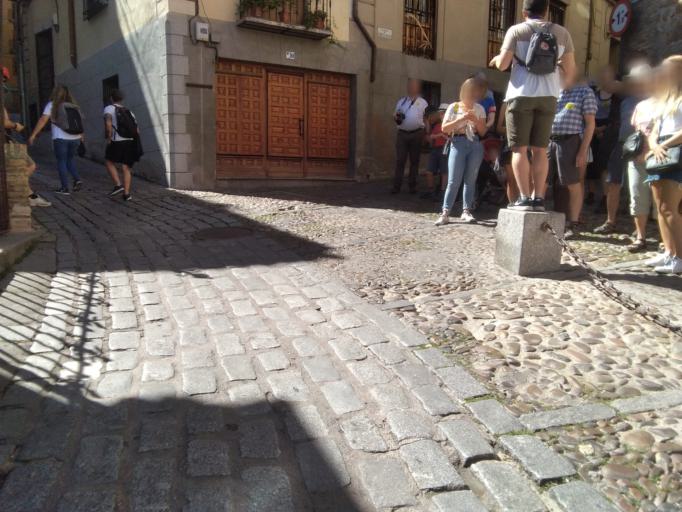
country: ES
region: Castille-La Mancha
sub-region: Province of Toledo
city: Toledo
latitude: 39.8605
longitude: -4.0243
